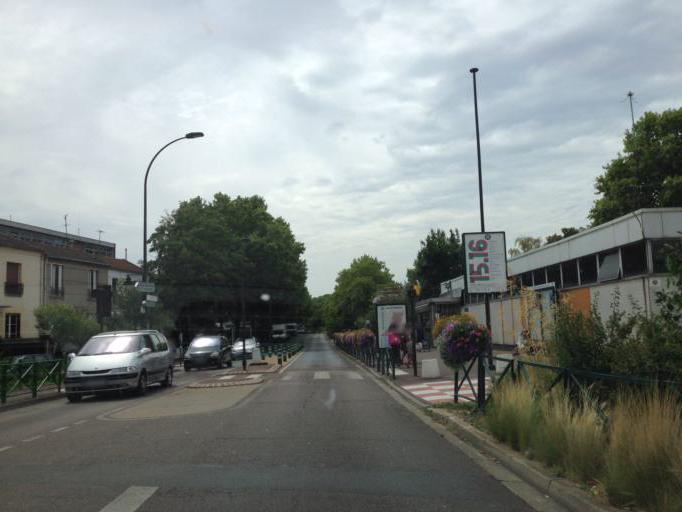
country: FR
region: Ile-de-France
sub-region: Departement des Hauts-de-Seine
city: Malakoff
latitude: 48.8227
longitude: 2.2991
